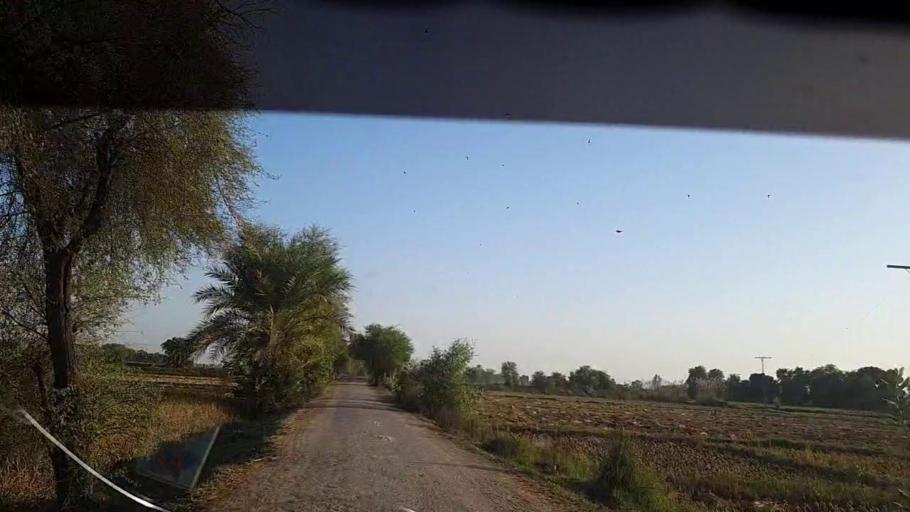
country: PK
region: Sindh
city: Ratodero
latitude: 27.8692
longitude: 68.1883
